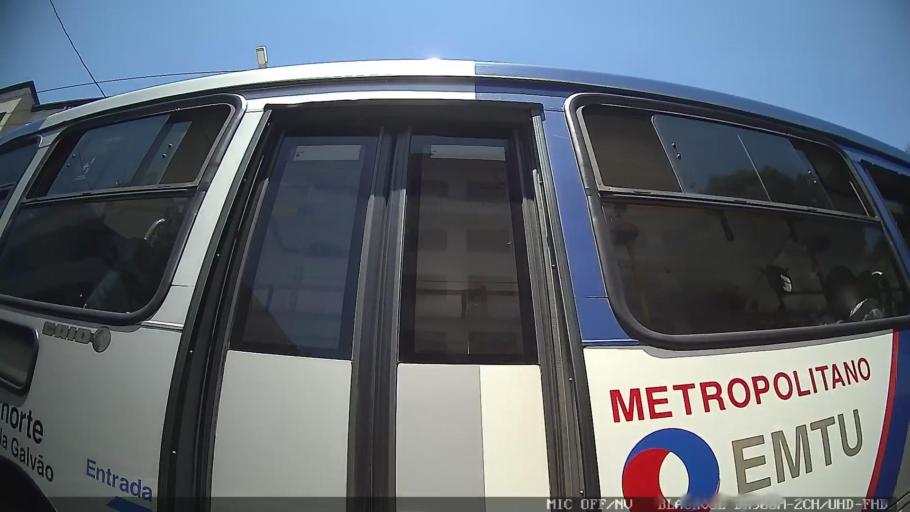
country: BR
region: Sao Paulo
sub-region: Guarulhos
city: Guarulhos
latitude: -23.5240
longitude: -46.5483
